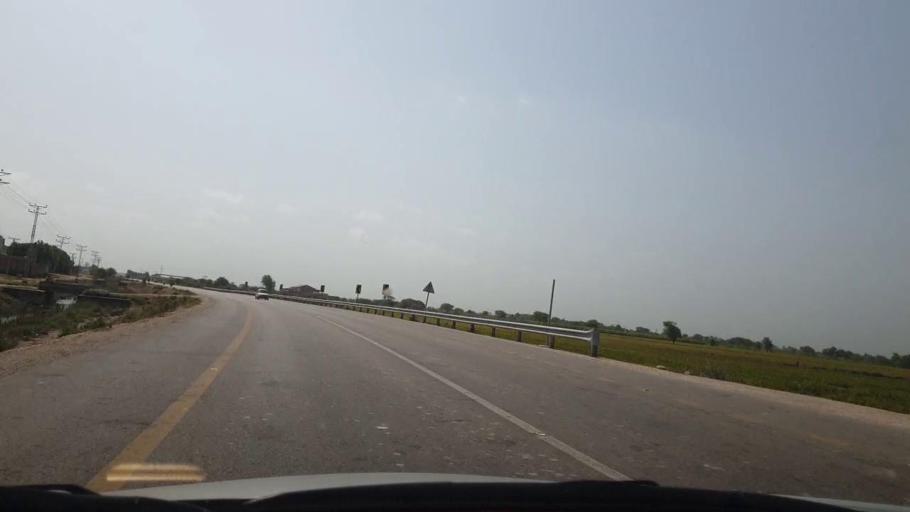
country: PK
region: Sindh
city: Matli
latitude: 25.0026
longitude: 68.6503
